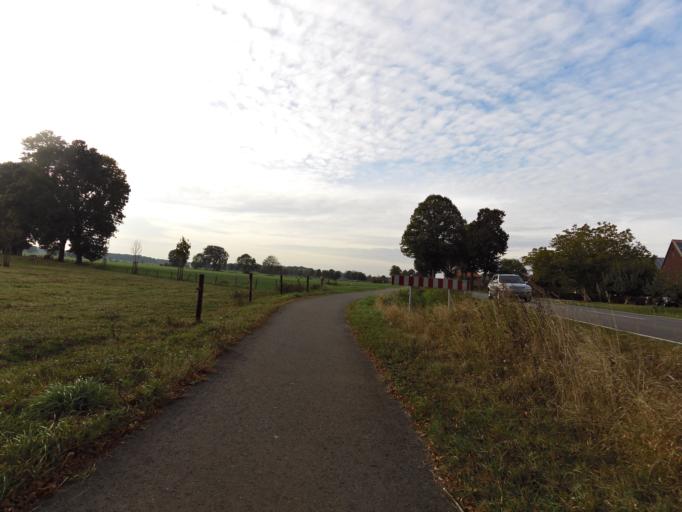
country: DE
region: North Rhine-Westphalia
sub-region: Regierungsbezirk Munster
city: Isselburg
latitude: 51.8013
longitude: 6.5140
